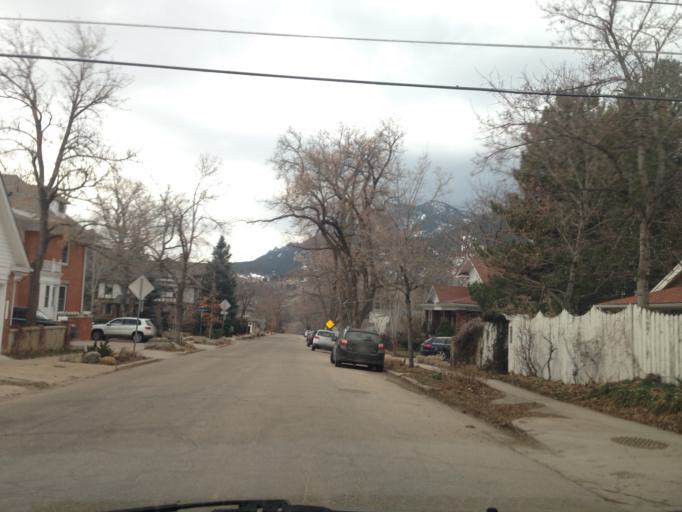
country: US
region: Colorado
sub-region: Boulder County
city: Boulder
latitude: 40.0202
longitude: -105.2916
